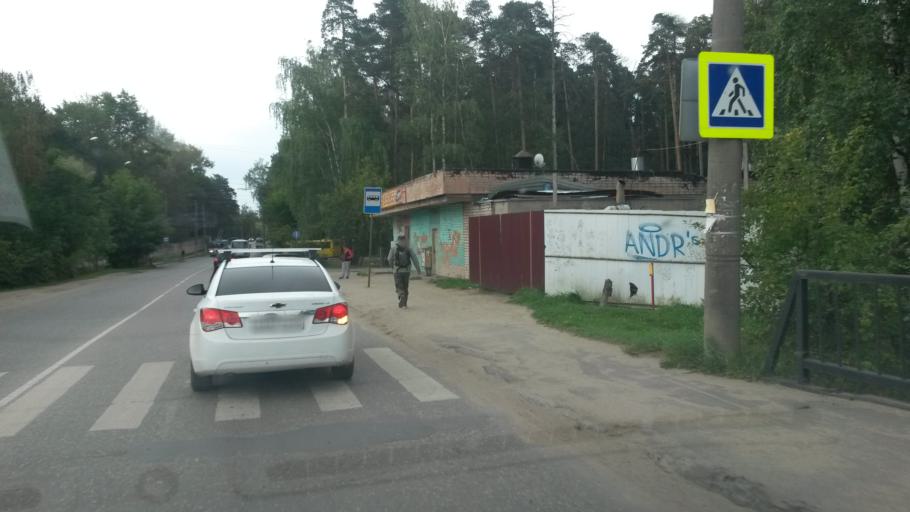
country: RU
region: Ivanovo
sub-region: Gorod Ivanovo
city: Ivanovo
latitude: 57.0261
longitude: 40.9383
